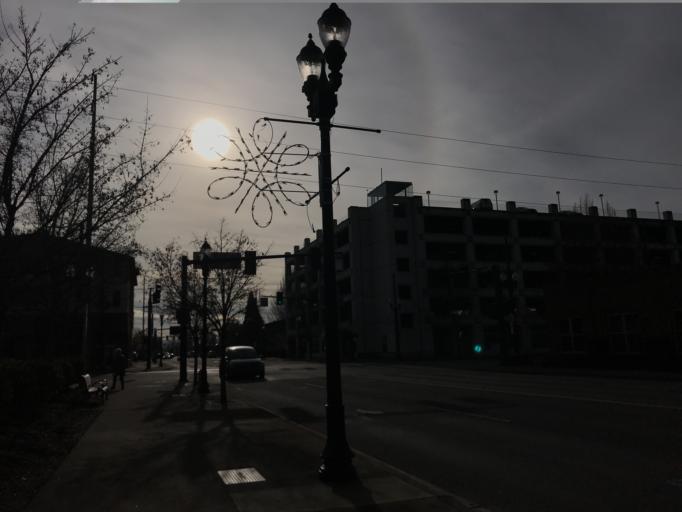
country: US
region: Oregon
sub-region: Washington County
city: Hillsboro
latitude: 45.5218
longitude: -122.9897
